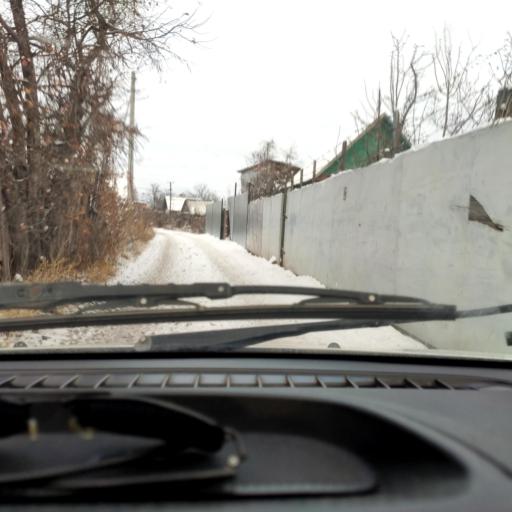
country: RU
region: Samara
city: Tol'yatti
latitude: 53.5383
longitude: 49.4279
